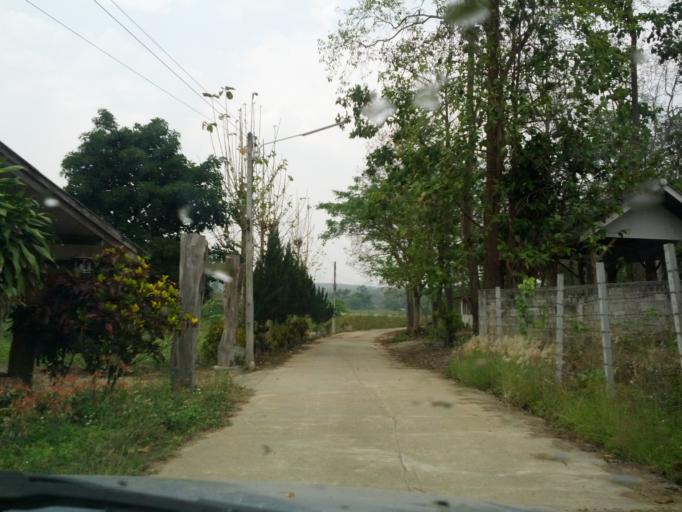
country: TH
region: Chiang Mai
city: Mae Taeng
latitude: 19.1064
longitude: 98.9904
